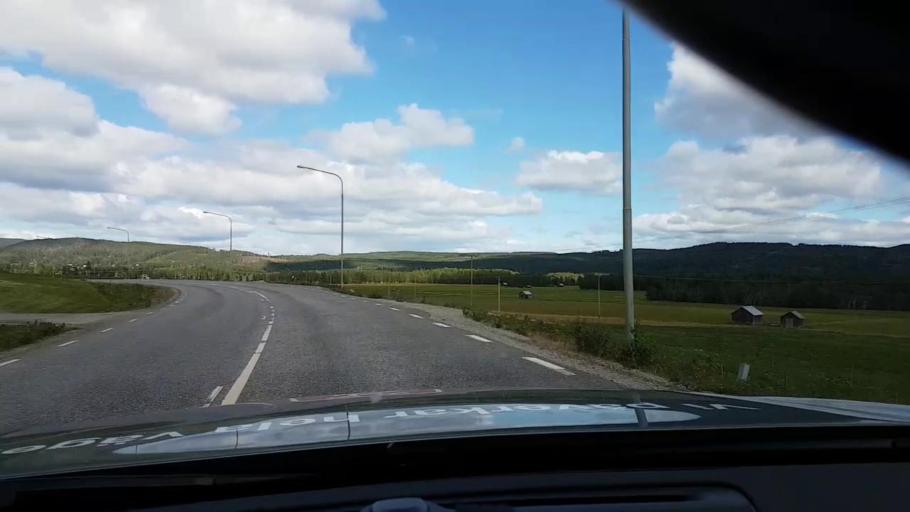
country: SE
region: Vaesternorrland
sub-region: OErnskoeldsviks Kommun
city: Bredbyn
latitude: 63.4971
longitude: 18.0829
